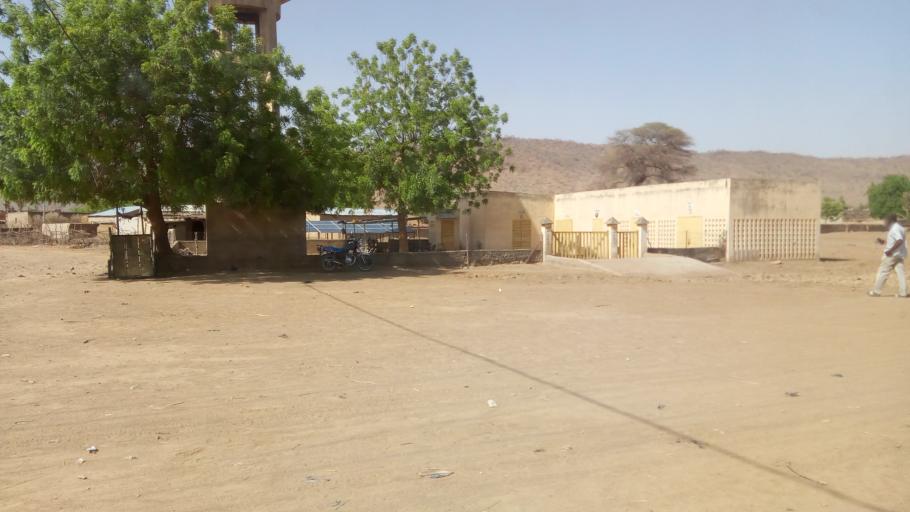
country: ML
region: Kayes
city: Yelimane
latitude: 14.6457
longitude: -10.7488
